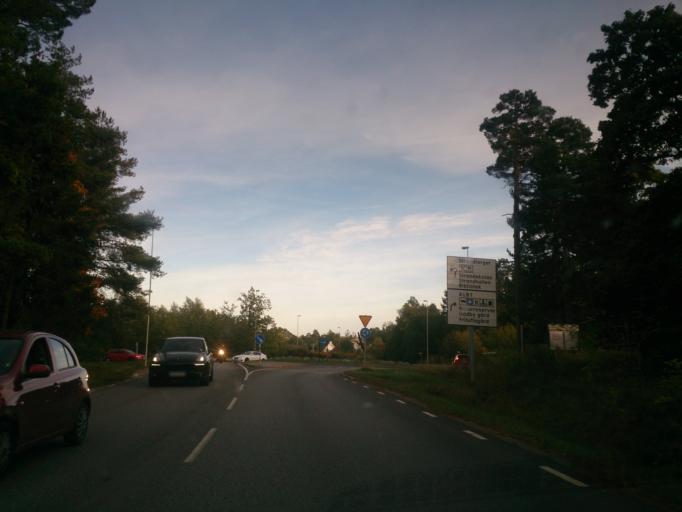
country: SE
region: Stockholm
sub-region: Nacka Kommun
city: Fisksatra
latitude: 59.2416
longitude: 18.2822
